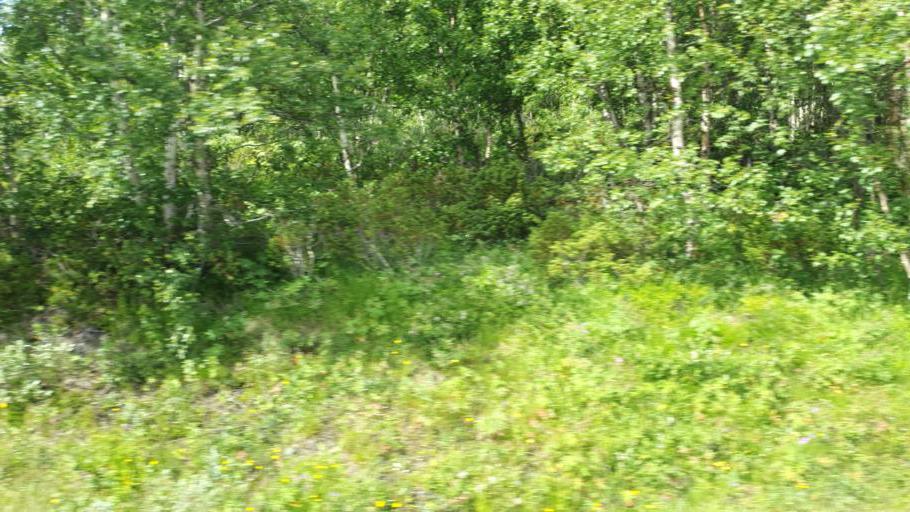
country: NO
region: Oppland
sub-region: Vaga
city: Vagamo
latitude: 61.5302
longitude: 8.8792
